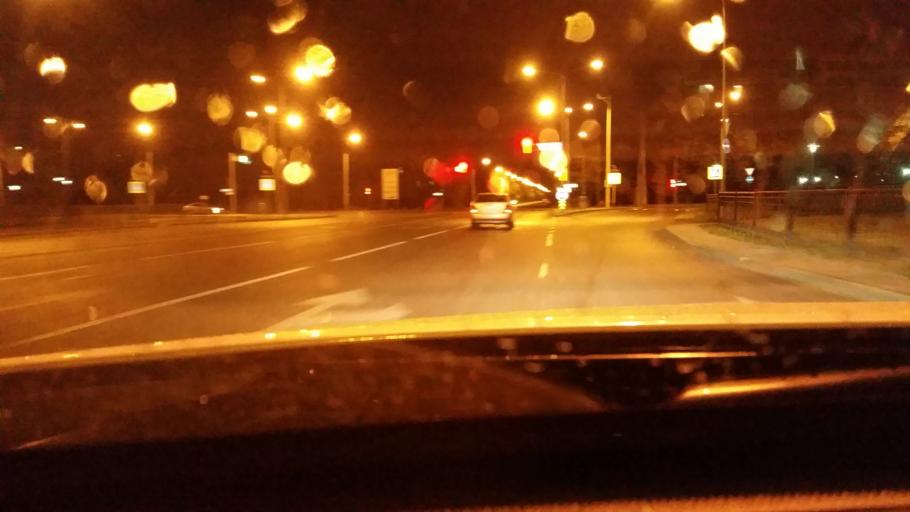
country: KZ
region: Astana Qalasy
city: Astana
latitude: 51.1566
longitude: 71.4779
